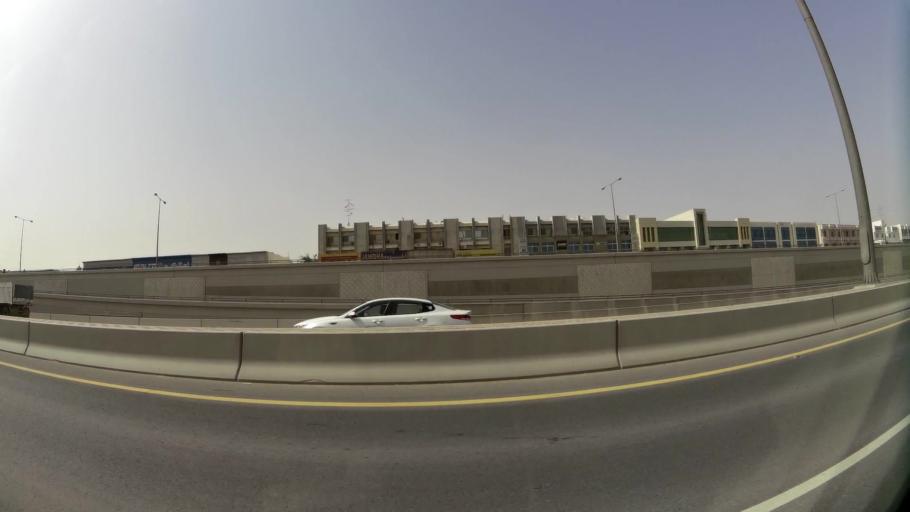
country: QA
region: Baladiyat ar Rayyan
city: Ar Rayyan
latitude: 25.2467
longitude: 51.4680
